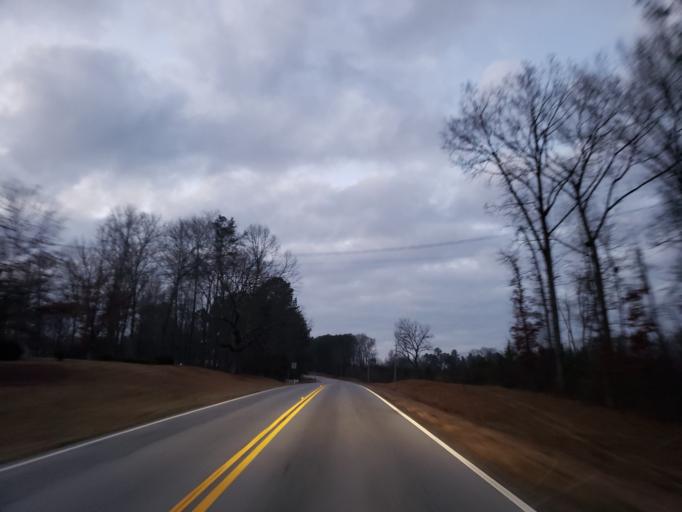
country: US
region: Georgia
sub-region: Carroll County
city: Temple
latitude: 33.7631
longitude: -85.0449
